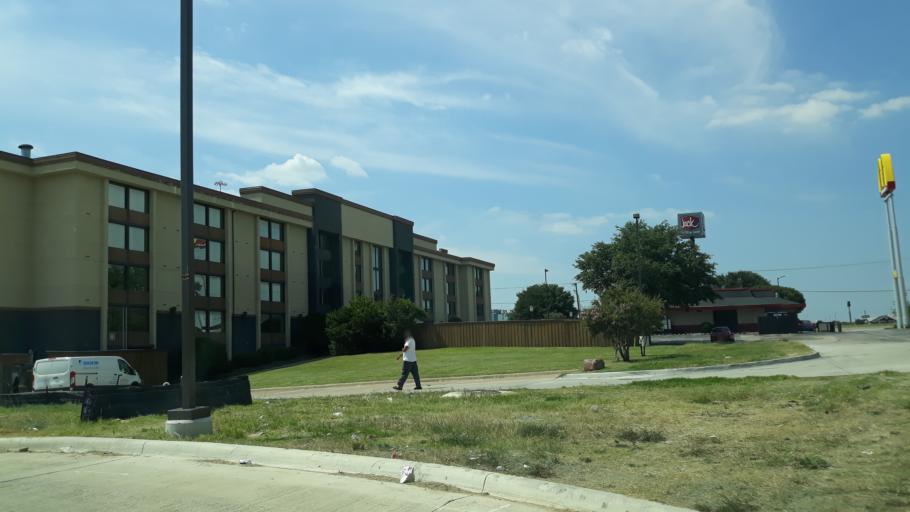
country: US
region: Texas
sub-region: Dallas County
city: Irving
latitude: 32.8348
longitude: -97.0108
